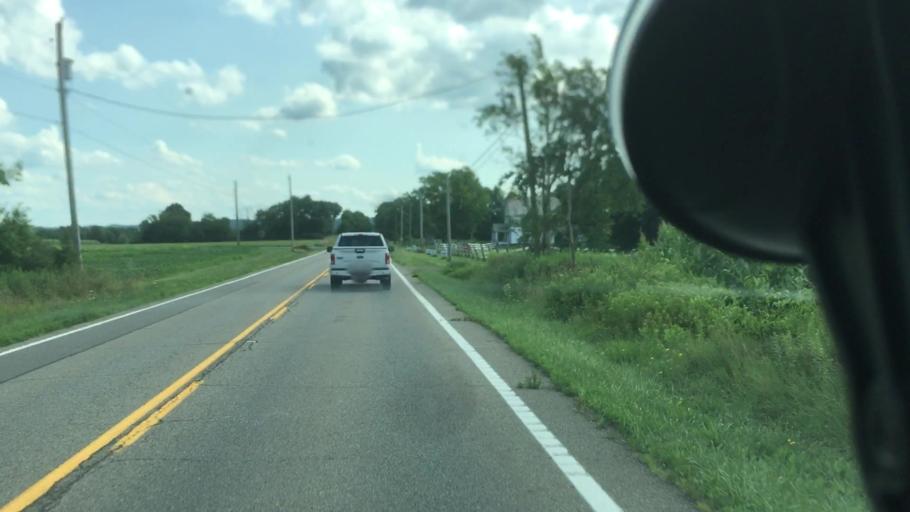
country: US
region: Ohio
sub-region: Columbiana County
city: Salem
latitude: 40.9671
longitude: -80.8294
